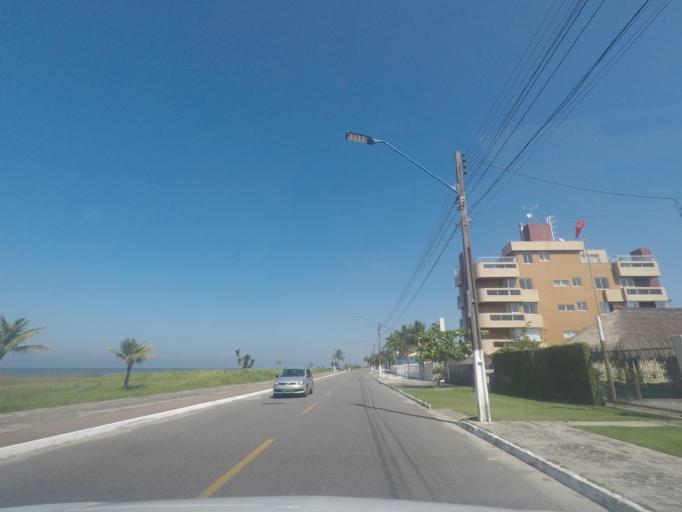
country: BR
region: Parana
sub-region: Pontal Do Parana
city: Pontal do Parana
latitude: -25.7263
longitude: -48.4860
